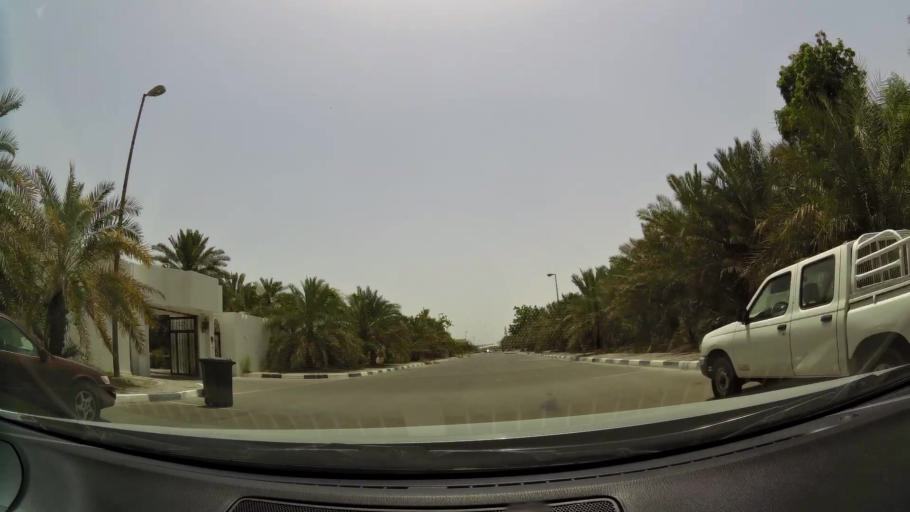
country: AE
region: Abu Dhabi
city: Al Ain
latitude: 24.2027
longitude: 55.7385
